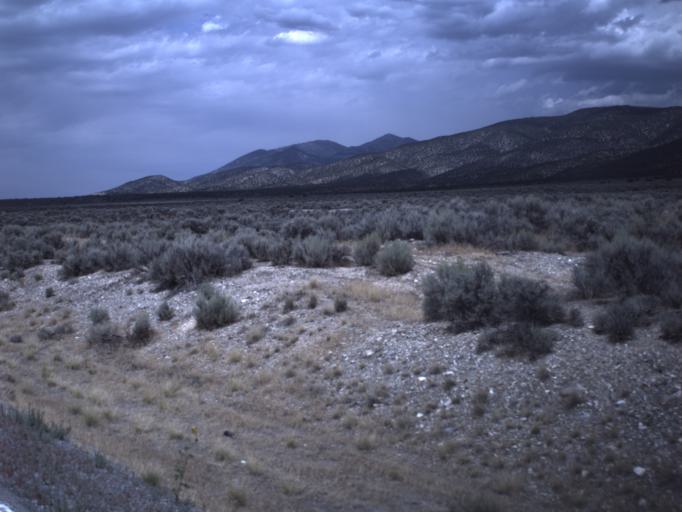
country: US
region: Utah
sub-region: Utah County
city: Eagle Mountain
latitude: 40.2758
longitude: -112.2513
